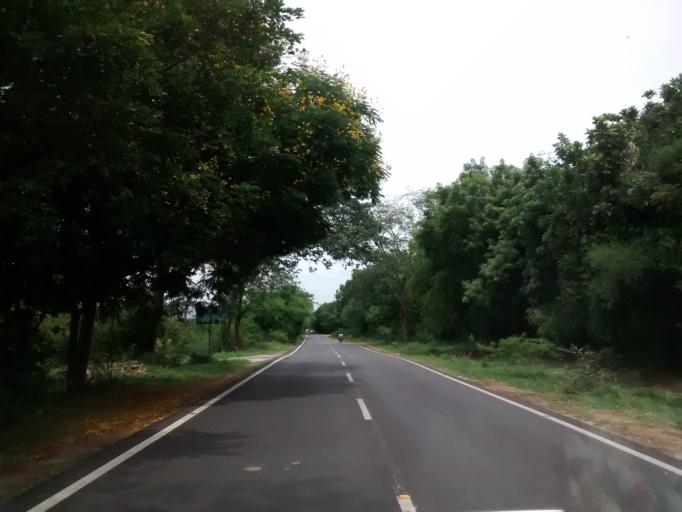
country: IN
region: Andhra Pradesh
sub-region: Chittoor
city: Tirupati
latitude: 13.6277
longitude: 79.3734
